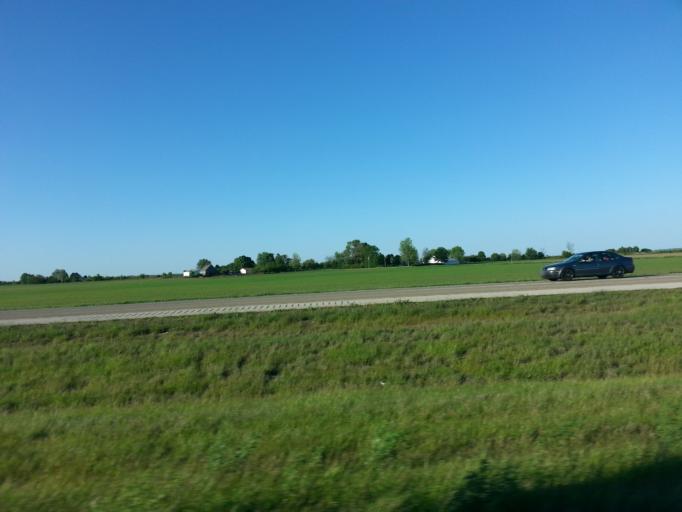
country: US
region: Illinois
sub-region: De Witt County
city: Farmer City
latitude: 40.2932
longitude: -88.7014
